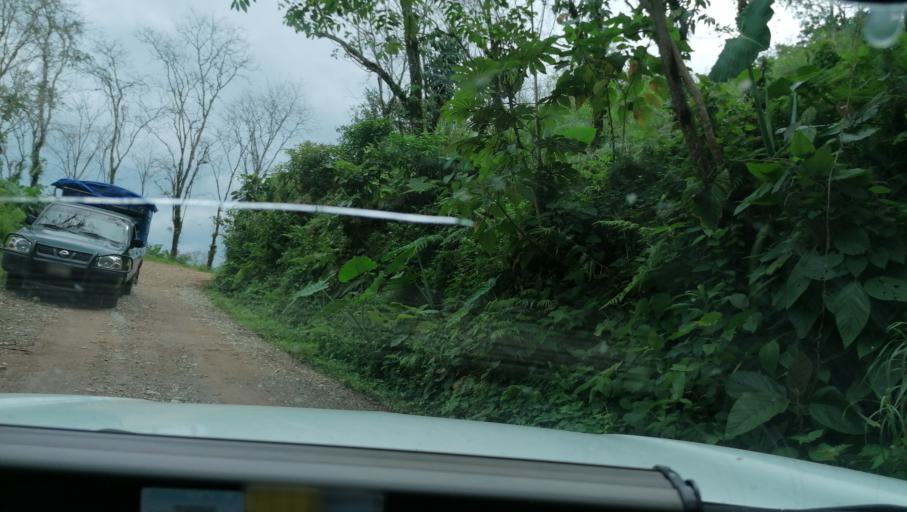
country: MX
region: Chiapas
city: Ixtacomitan
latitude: 17.3512
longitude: -93.1450
